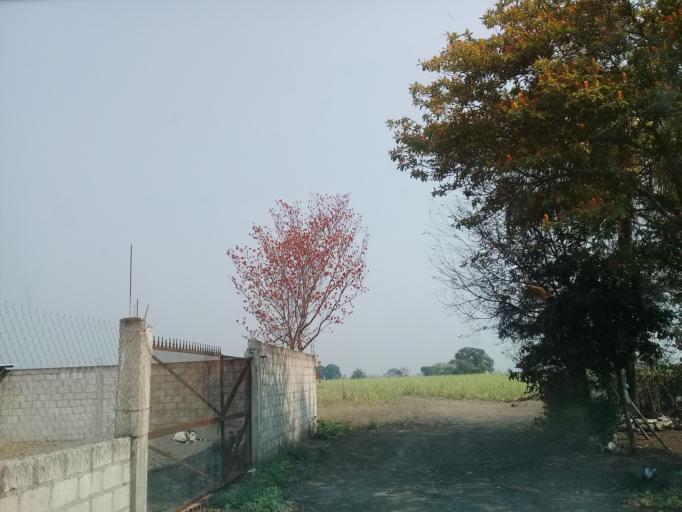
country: MX
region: Oaxaca
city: Acatlan de Perez Figueroa
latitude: 18.6083
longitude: -96.5752
